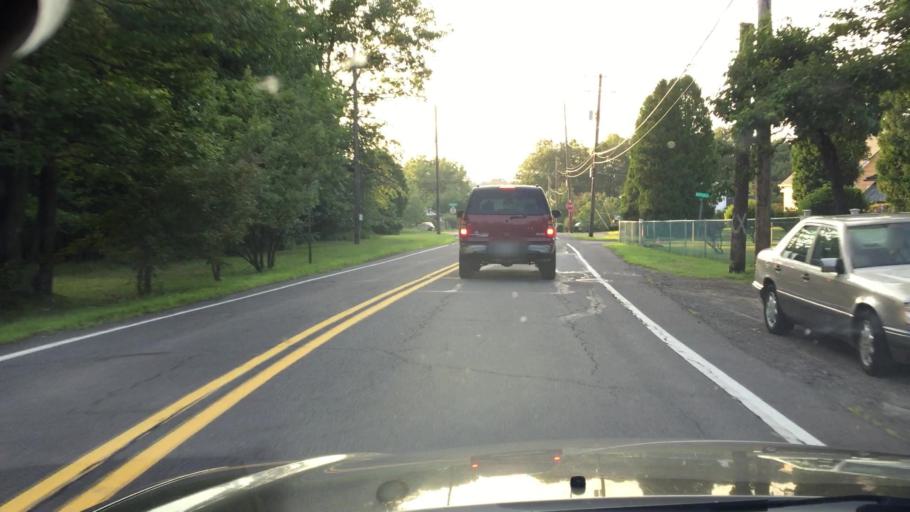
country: US
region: Pennsylvania
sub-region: Luzerne County
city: Harleigh
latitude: 40.9896
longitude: -75.9794
